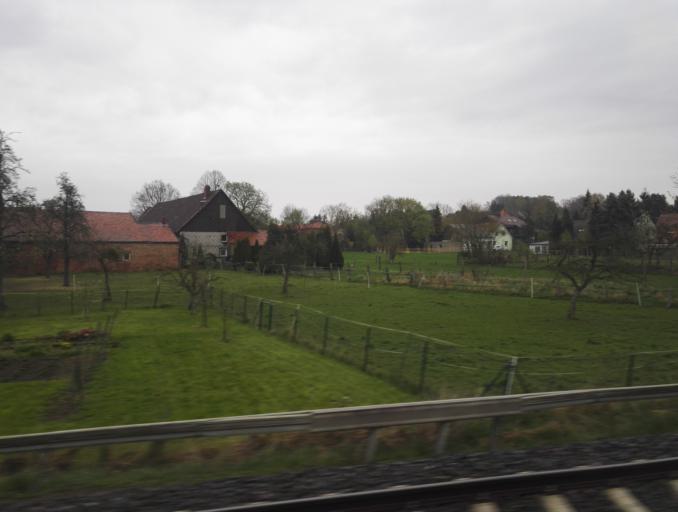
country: DE
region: Lower Saxony
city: Baddeckenstedt
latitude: 52.0930
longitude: 10.2094
